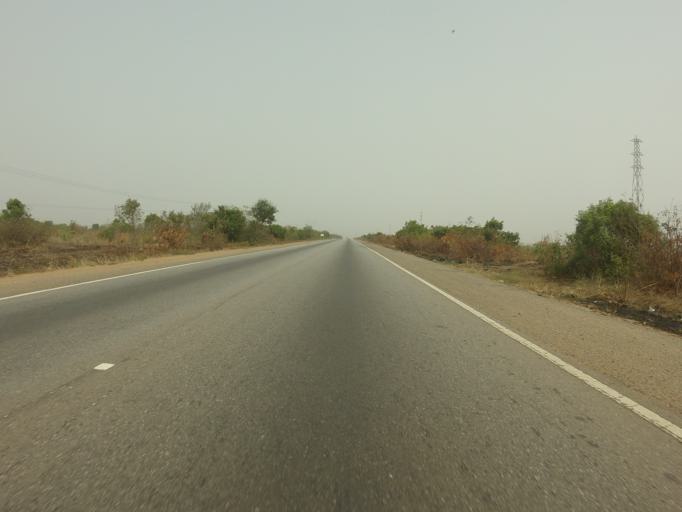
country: GH
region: Greater Accra
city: Tema
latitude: 5.8053
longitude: 0.1494
